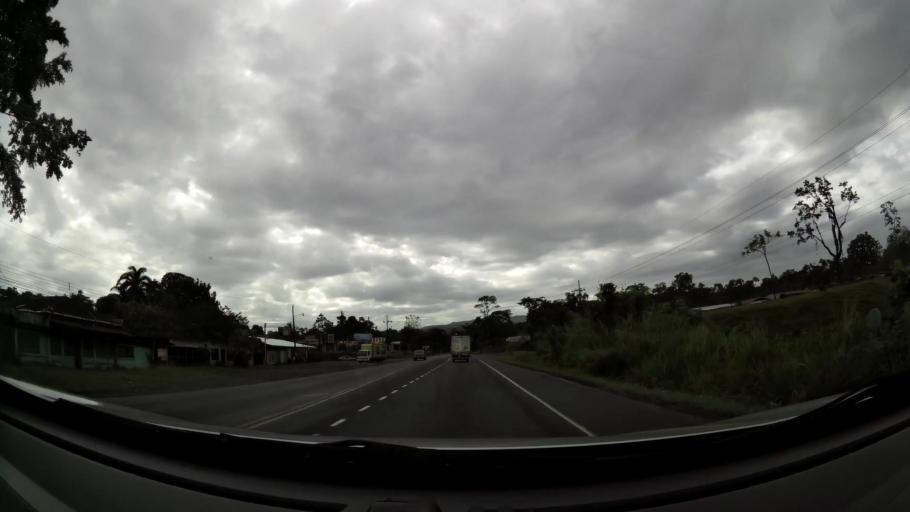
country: CR
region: Limon
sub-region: Canton de Siquirres
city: Siquirres
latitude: 10.1287
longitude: -83.5595
